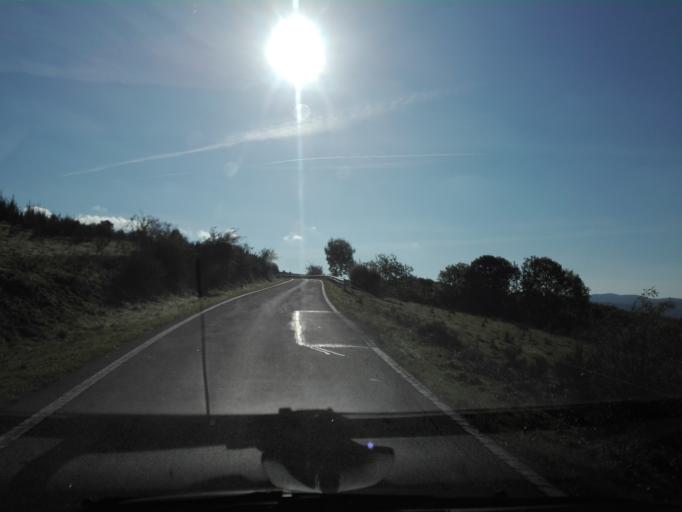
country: ES
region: Navarre
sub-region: Provincia de Navarra
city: Oronz
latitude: 42.9506
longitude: -1.1187
